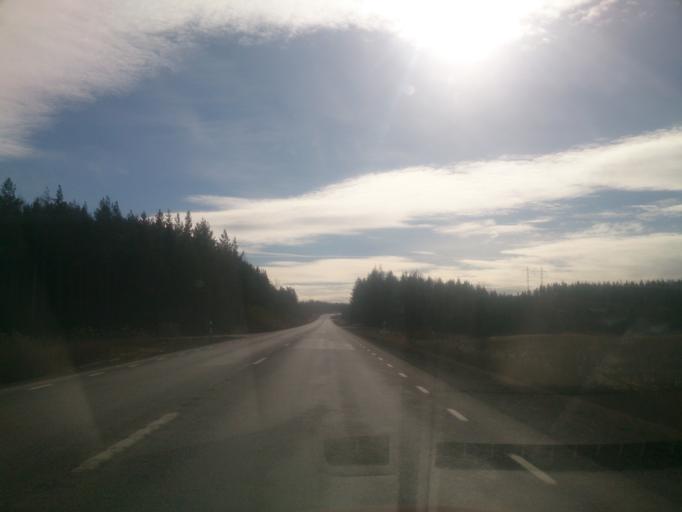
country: SE
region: OEstergoetland
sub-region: Norrkopings Kommun
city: Kimstad
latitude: 58.5283
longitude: 15.9805
